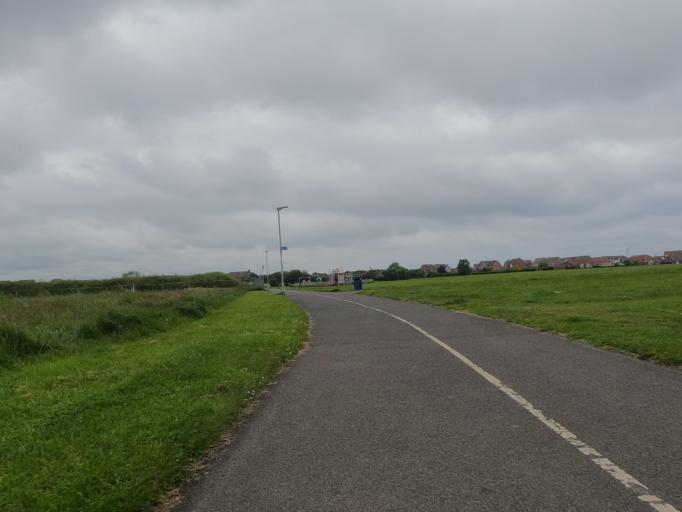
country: GB
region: England
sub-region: Northumberland
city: Blyth
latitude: 55.1079
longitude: -1.5207
